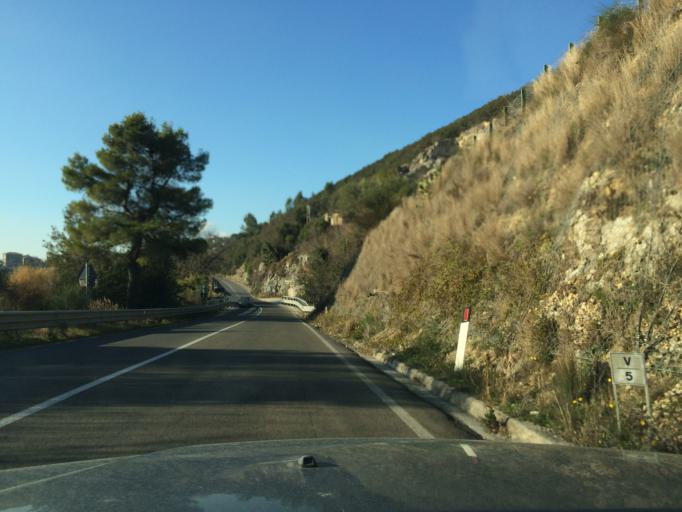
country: IT
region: Umbria
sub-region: Provincia di Terni
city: Fornole
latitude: 42.5412
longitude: 12.4656
